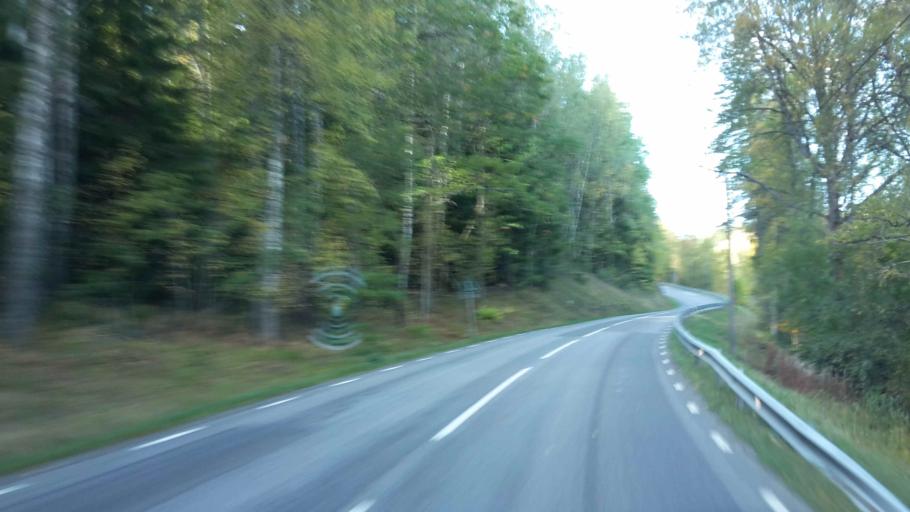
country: SE
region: OEstergoetland
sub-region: Atvidabergs Kommun
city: Atvidaberg
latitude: 58.1760
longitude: 16.1222
